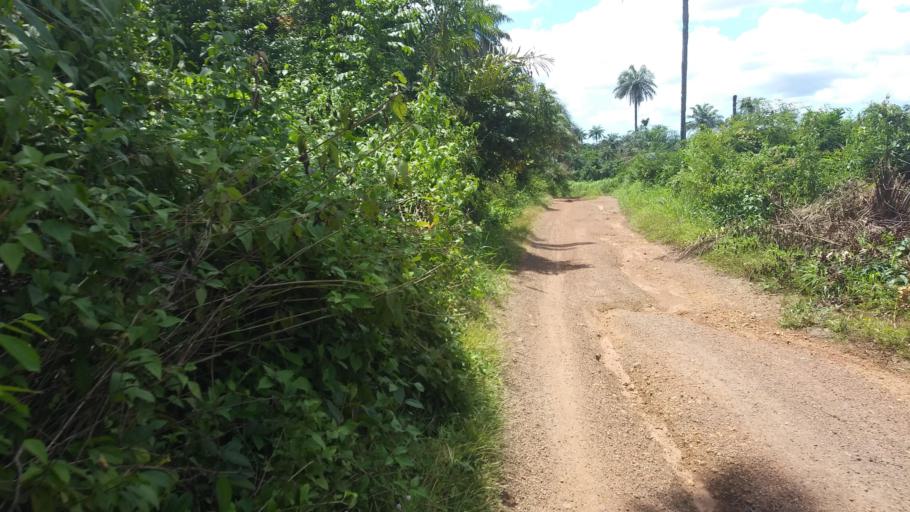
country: SL
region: Northern Province
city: Binkolo
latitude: 8.8795
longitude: -11.9627
